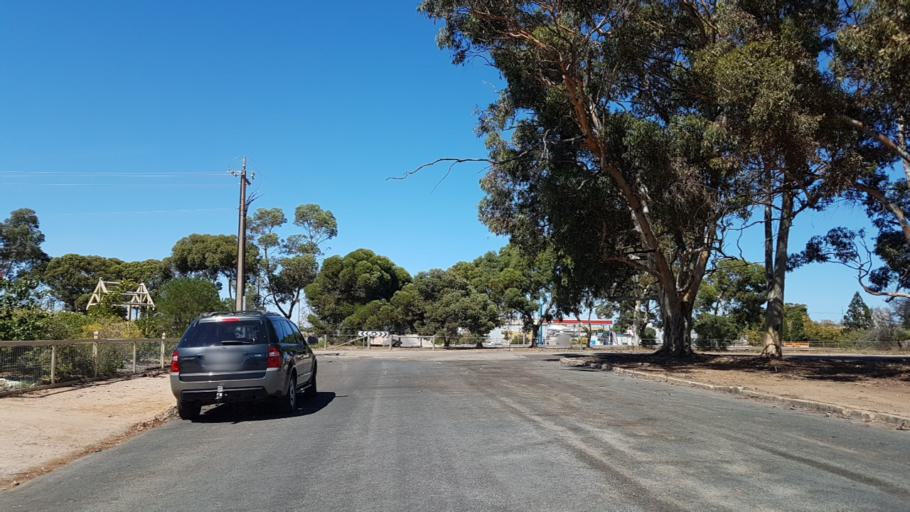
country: AU
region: South Australia
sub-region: Copper Coast
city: Kadina
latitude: -33.9656
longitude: 137.7190
